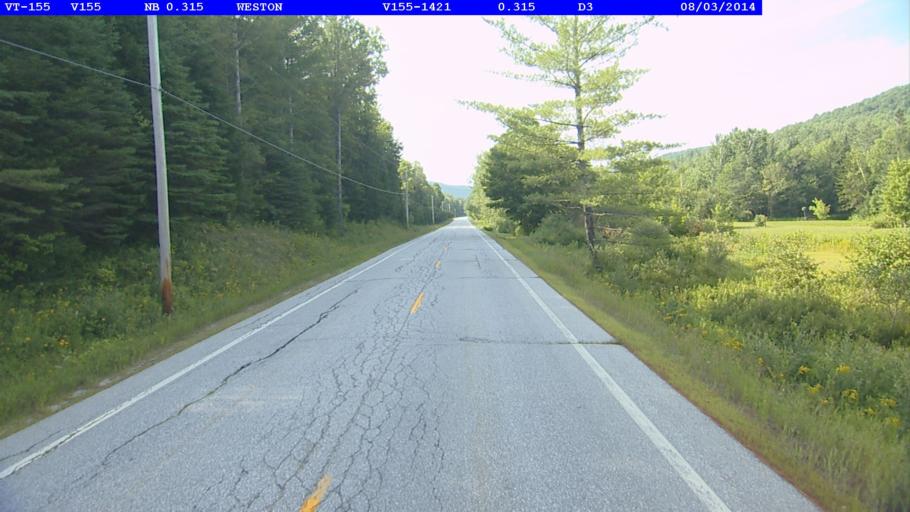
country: US
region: Vermont
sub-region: Windsor County
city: Chester
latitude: 43.3411
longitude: -72.7879
